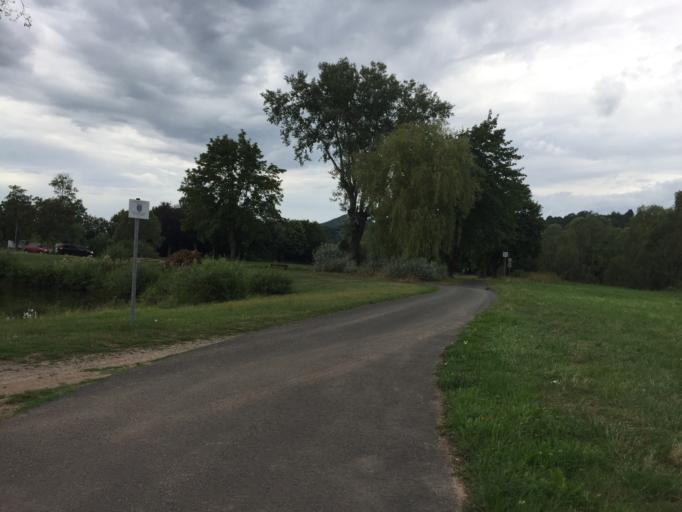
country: DE
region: Hesse
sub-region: Regierungsbezirk Kassel
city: Rotenburg an der Fulda
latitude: 50.9874
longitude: 9.7597
